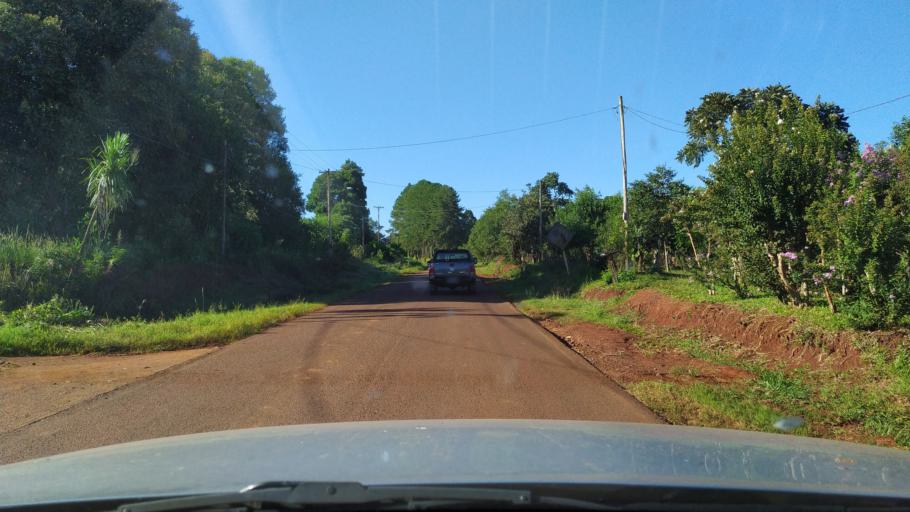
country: AR
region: Misiones
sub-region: Departamento de Montecarlo
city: Montecarlo
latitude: -26.6019
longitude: -54.7021
